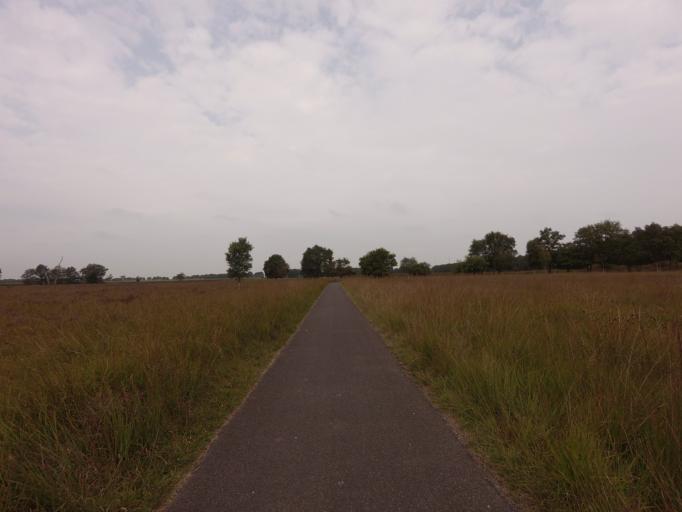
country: NL
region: Drenthe
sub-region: Gemeente Westerveld
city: Dwingeloo
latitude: 52.8833
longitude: 6.4612
